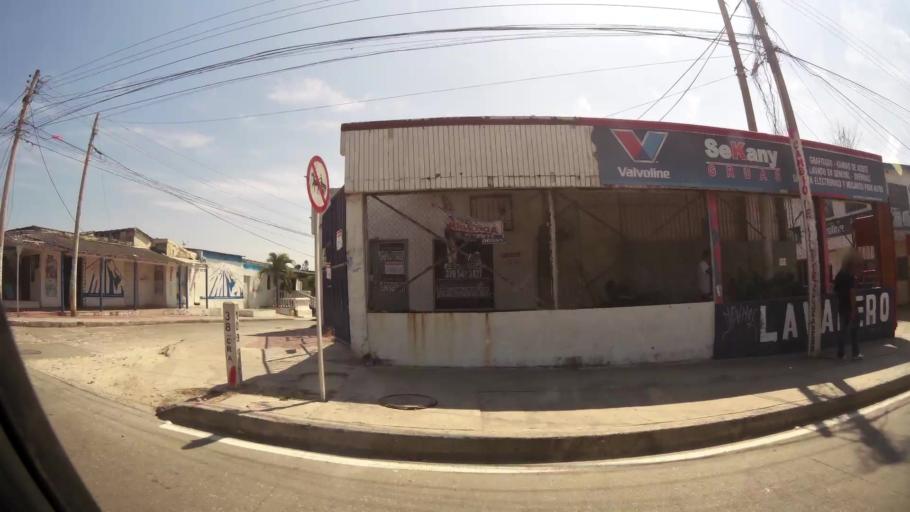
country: CO
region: Atlantico
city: Barranquilla
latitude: 10.9827
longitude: -74.8355
